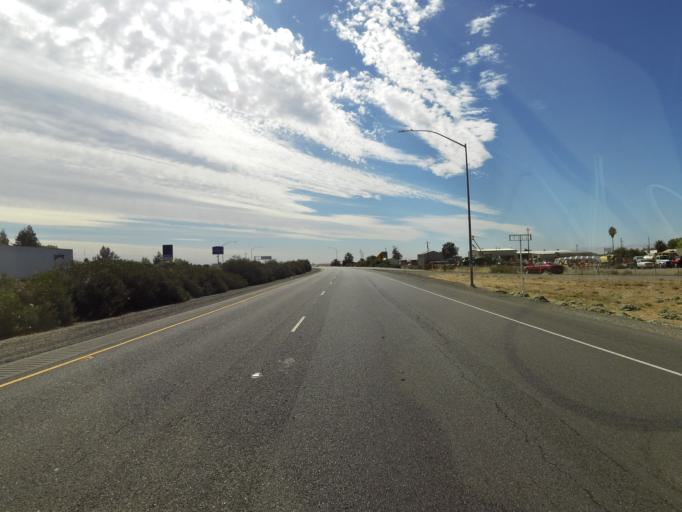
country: US
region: California
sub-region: Glenn County
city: Willows
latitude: 39.5235
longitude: -122.2149
